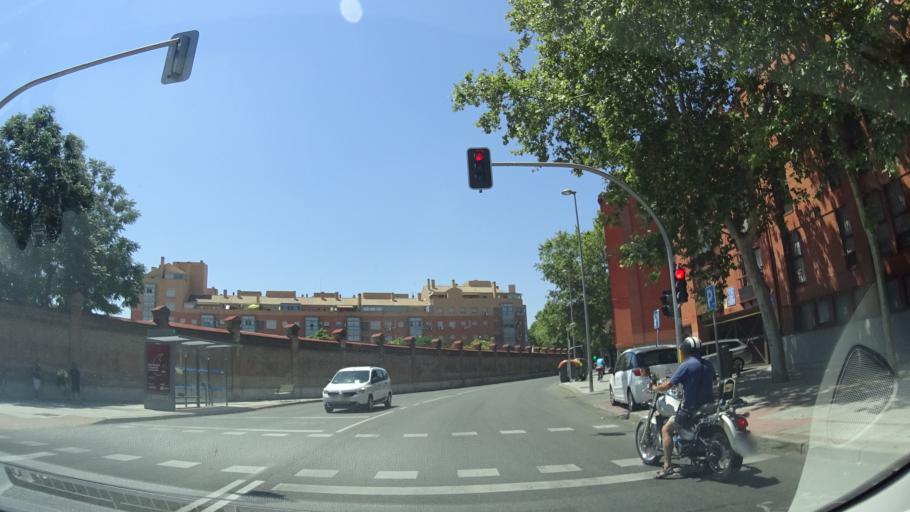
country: ES
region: Madrid
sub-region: Provincia de Madrid
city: Latina
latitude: 40.3808
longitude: -3.7449
